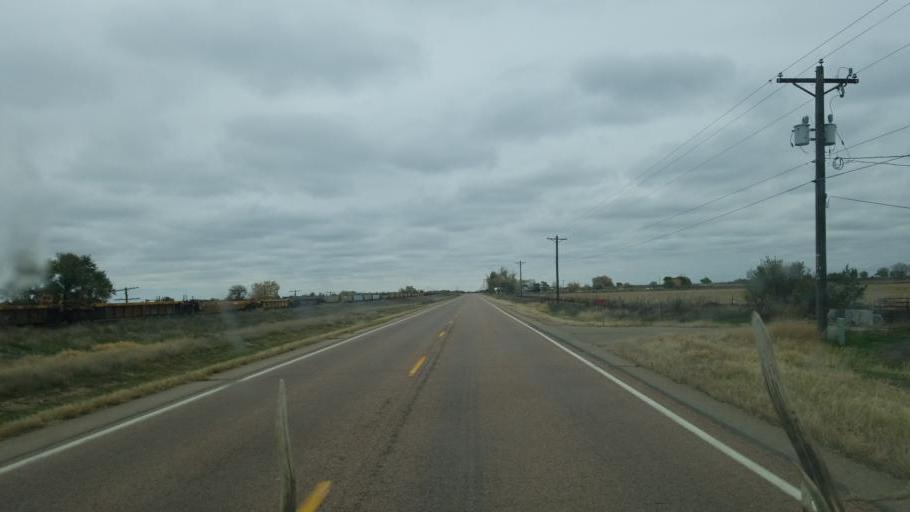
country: US
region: Colorado
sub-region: Crowley County
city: Ordway
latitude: 38.1847
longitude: -103.8816
